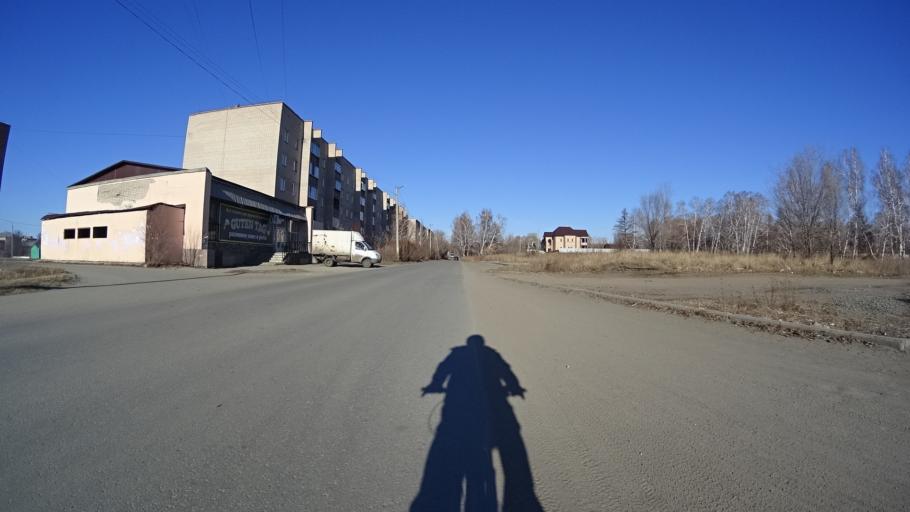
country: RU
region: Chelyabinsk
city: Troitsk
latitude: 54.0480
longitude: 61.6406
